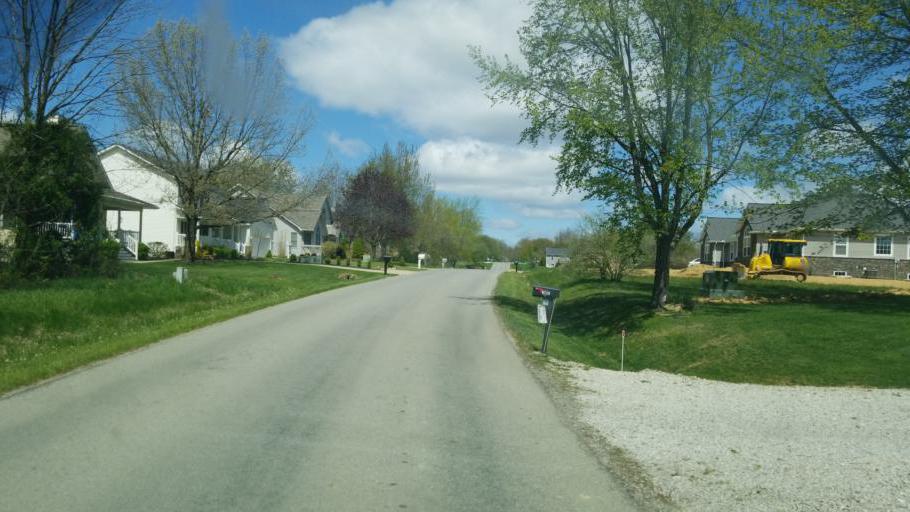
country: US
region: Ohio
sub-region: Knox County
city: Gambier
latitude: 40.4406
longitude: -82.3612
